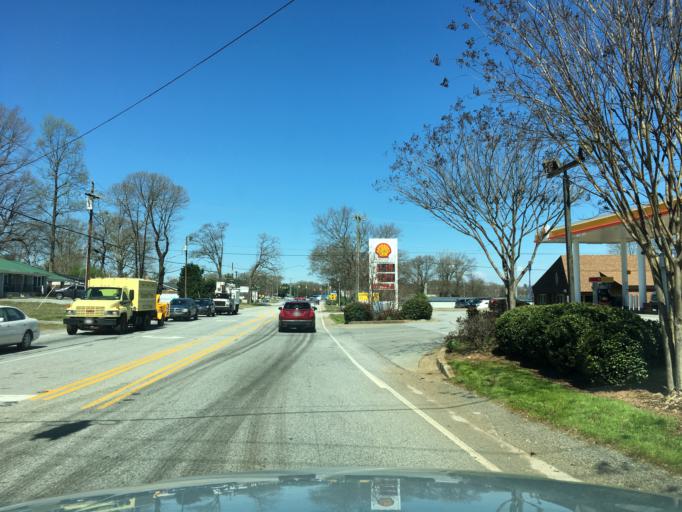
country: US
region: South Carolina
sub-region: Spartanburg County
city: Fairforest
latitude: 34.9328
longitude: -82.0021
